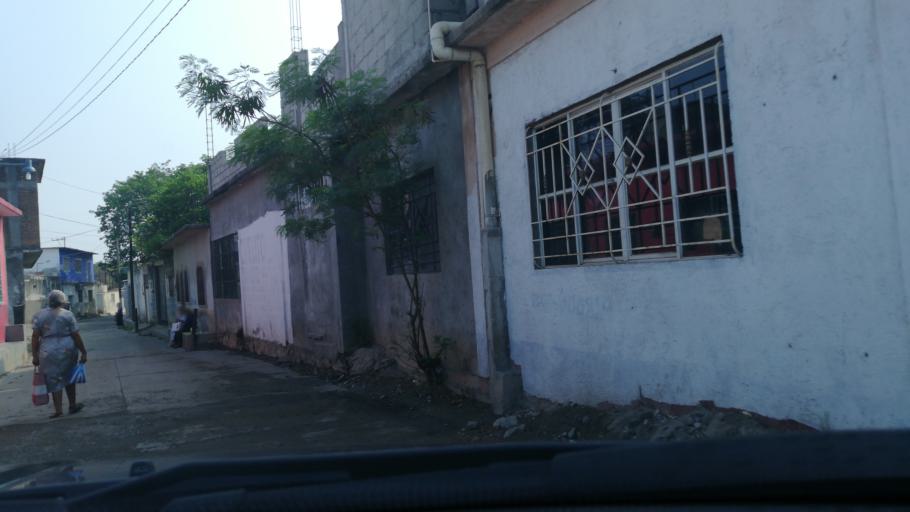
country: MX
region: Oaxaca
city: San Blas Atempa
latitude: 16.3356
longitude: -95.2268
